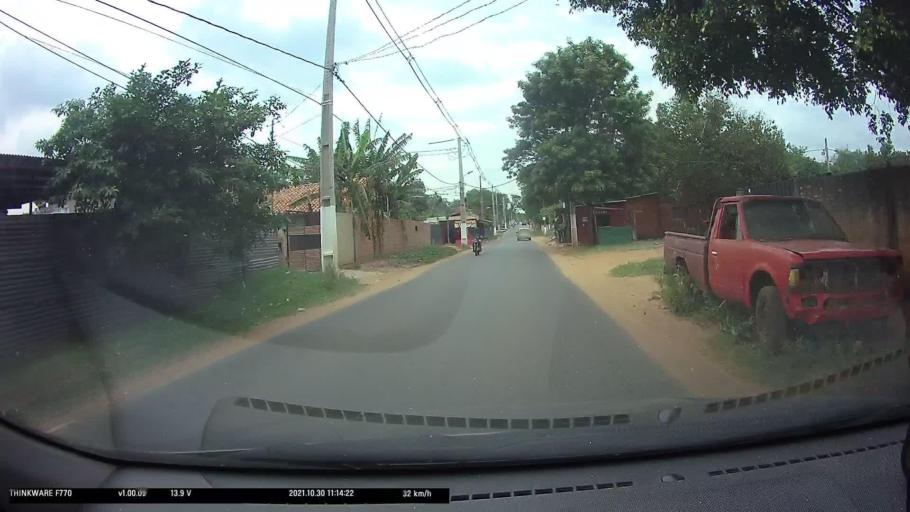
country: PY
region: Central
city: San Lorenzo
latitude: -25.3110
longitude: -57.5114
